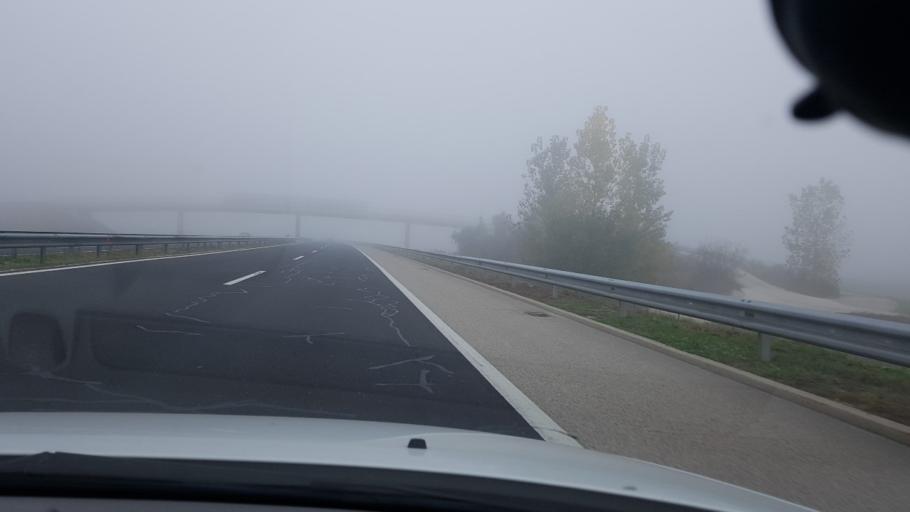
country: SI
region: Brezice
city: Brezice
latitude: 45.8975
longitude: 15.5792
